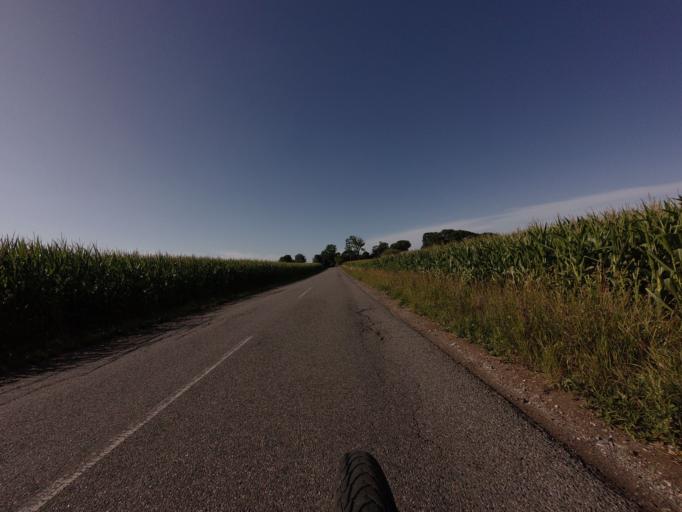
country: DK
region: North Denmark
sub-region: Hjorring Kommune
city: Vra
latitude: 57.3789
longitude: 10.0063
